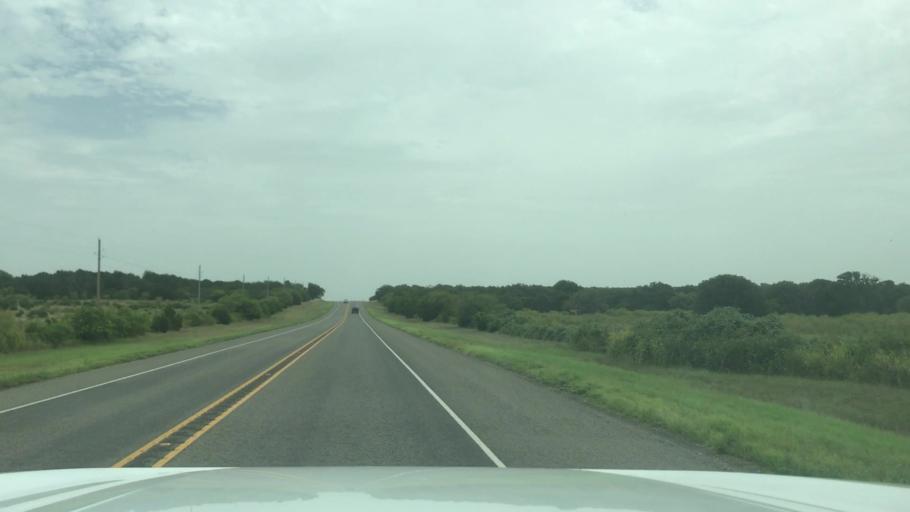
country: US
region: Texas
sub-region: Hamilton County
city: Hico
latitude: 31.9818
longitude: -97.9987
